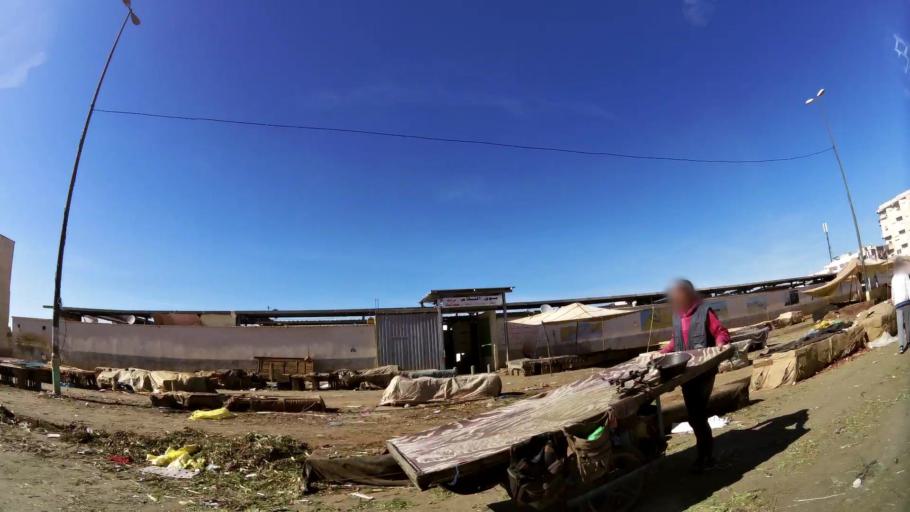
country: MA
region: Fes-Boulemane
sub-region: Fes
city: Fes
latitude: 34.0182
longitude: -4.9658
